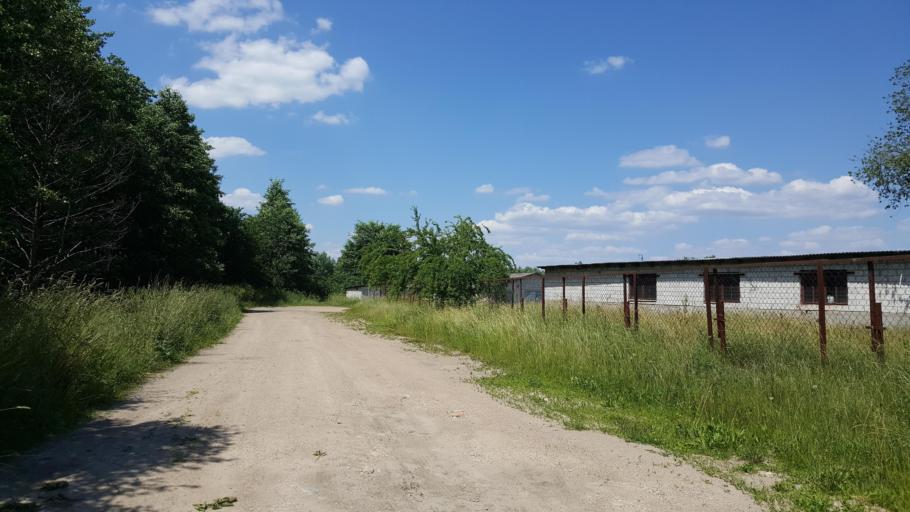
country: BY
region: Brest
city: Kamyanyets
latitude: 52.4104
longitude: 23.8271
